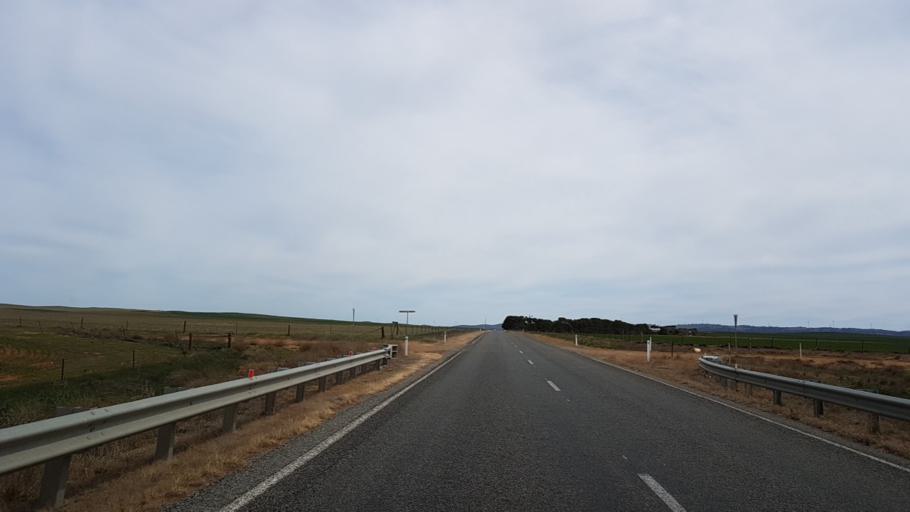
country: AU
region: South Australia
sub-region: Peterborough
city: Peterborough
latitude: -33.0169
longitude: 138.6945
